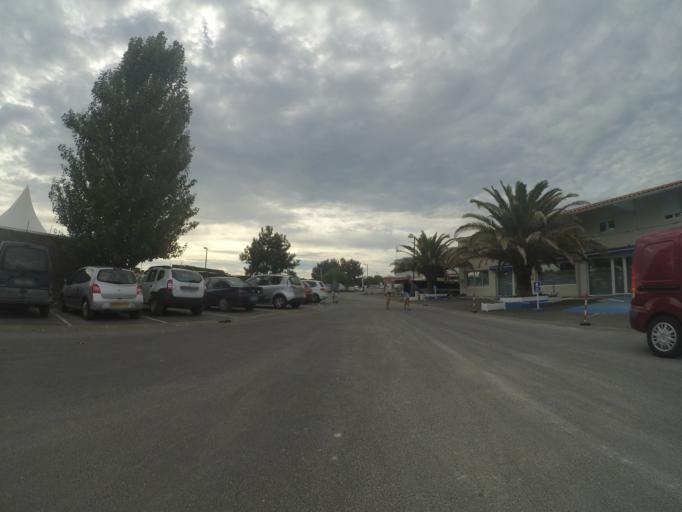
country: FR
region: Poitou-Charentes
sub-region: Departement de la Charente-Maritime
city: Meschers-sur-Gironde
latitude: 45.5554
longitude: -0.9435
